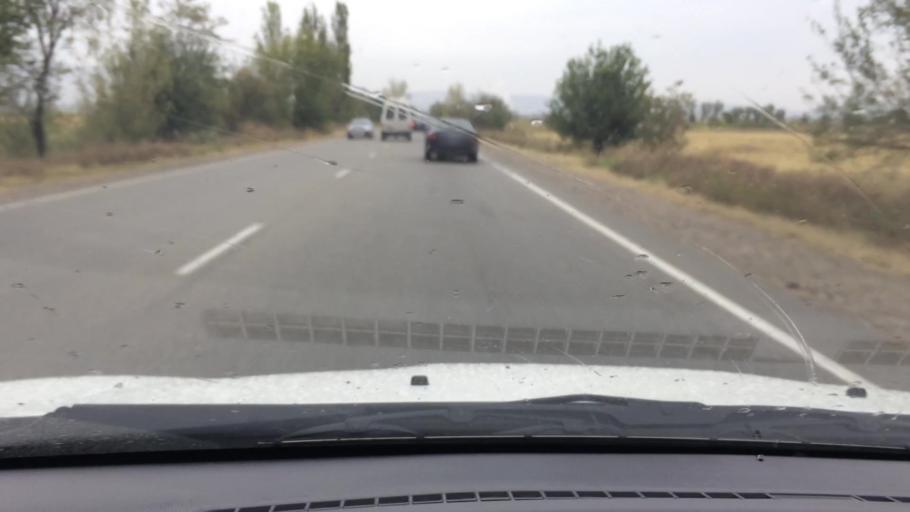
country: GE
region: Kvemo Kartli
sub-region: Marneuli
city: Marneuli
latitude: 41.5548
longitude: 44.7762
